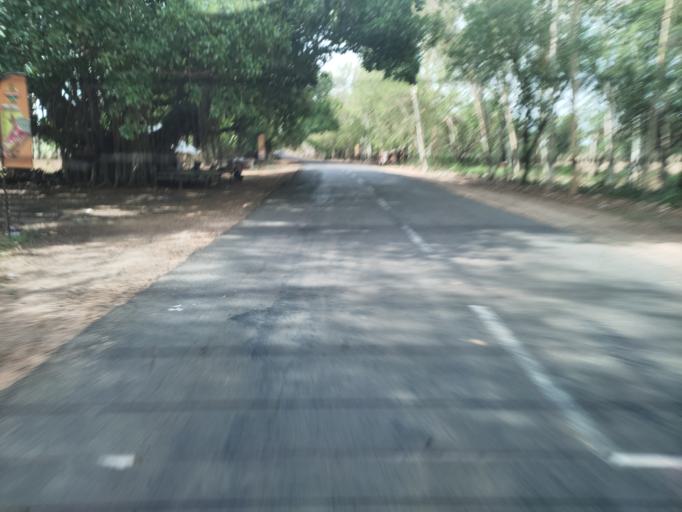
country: MM
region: Magway
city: Magway
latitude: 20.2273
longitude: 95.0185
